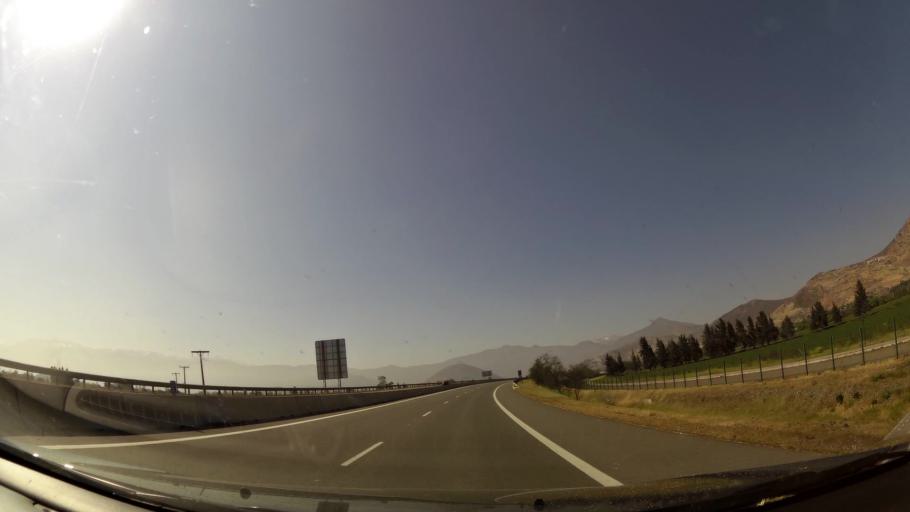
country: CL
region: Santiago Metropolitan
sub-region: Provincia de Chacabuco
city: Chicureo Abajo
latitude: -33.2920
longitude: -70.6944
